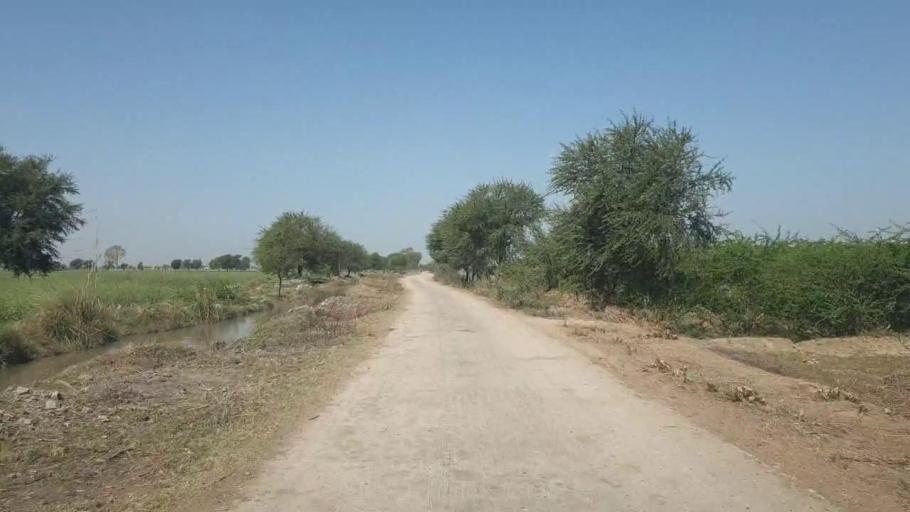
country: PK
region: Sindh
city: Umarkot
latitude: 25.2985
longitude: 69.6240
